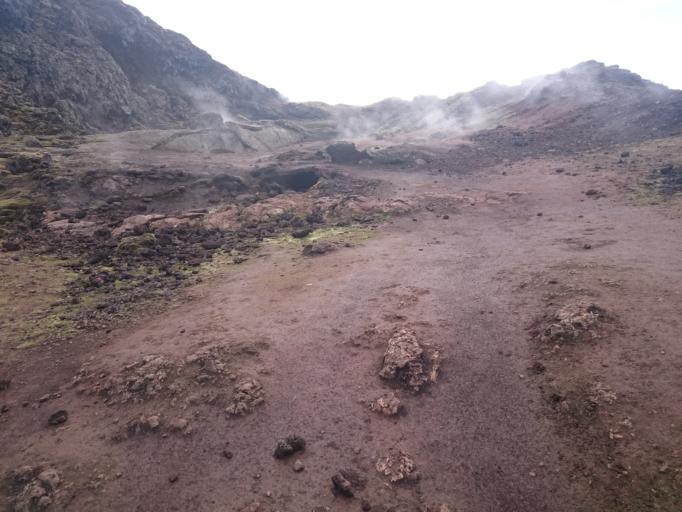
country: IS
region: Northeast
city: Laugar
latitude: 65.7206
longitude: -16.7941
